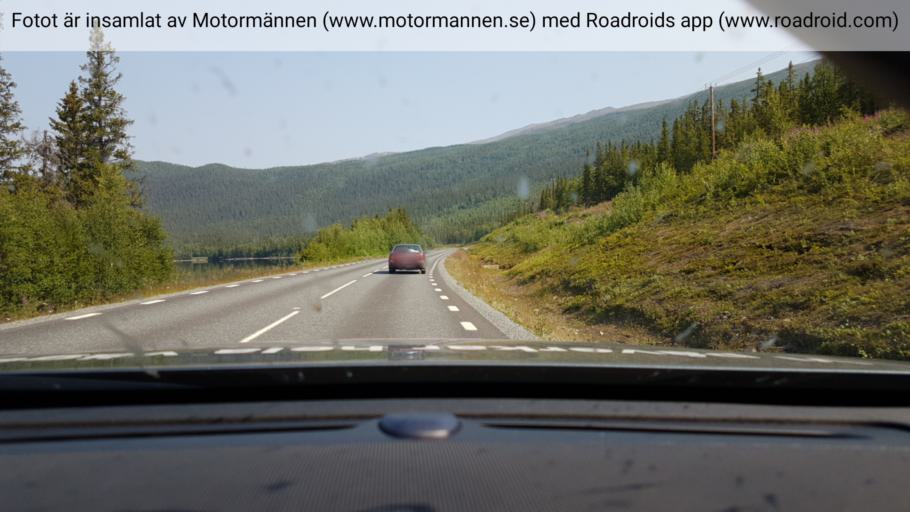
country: SE
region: Vaesterbotten
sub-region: Vilhelmina Kommun
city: Sjoberg
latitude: 65.6218
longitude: 15.5357
